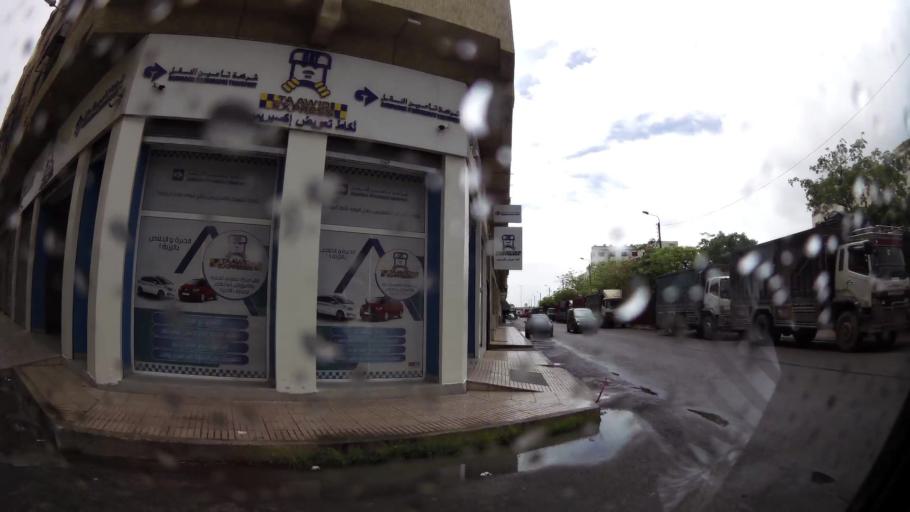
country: MA
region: Grand Casablanca
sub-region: Casablanca
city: Casablanca
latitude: 33.5813
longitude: -7.5992
